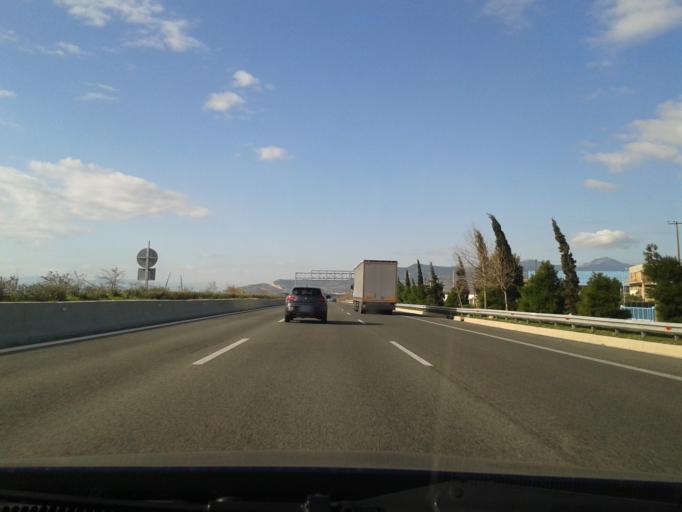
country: GR
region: Attica
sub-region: Nomarchia Dytikis Attikis
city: Nea Peramos
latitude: 38.0086
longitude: 23.4011
